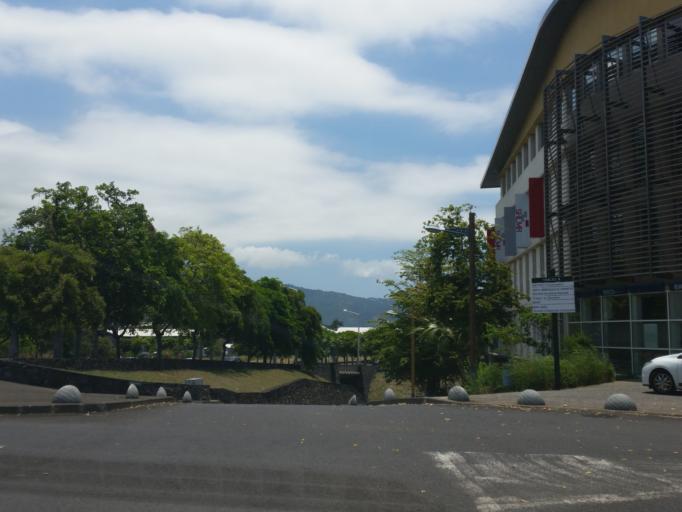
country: RE
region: Reunion
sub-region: Reunion
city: Sainte-Marie
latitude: -20.9024
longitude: 55.5001
